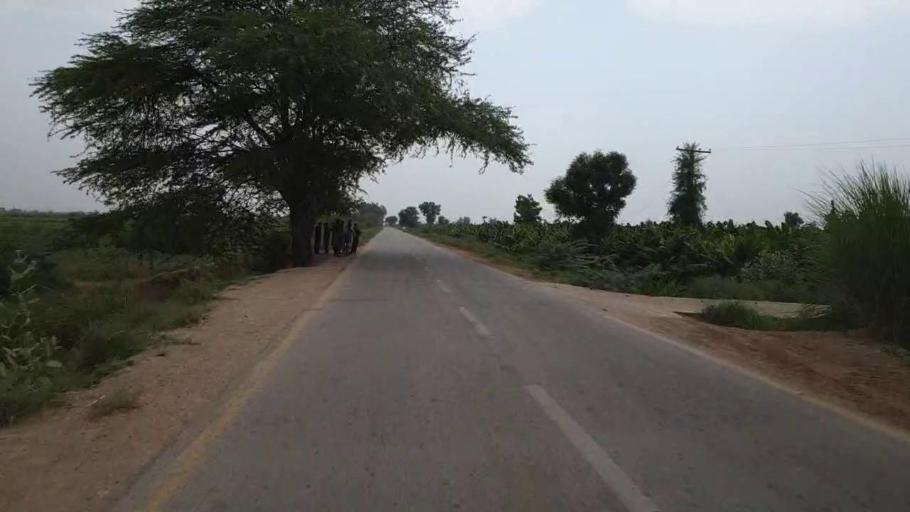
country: PK
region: Sindh
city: Bandhi
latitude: 26.5887
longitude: 68.2201
